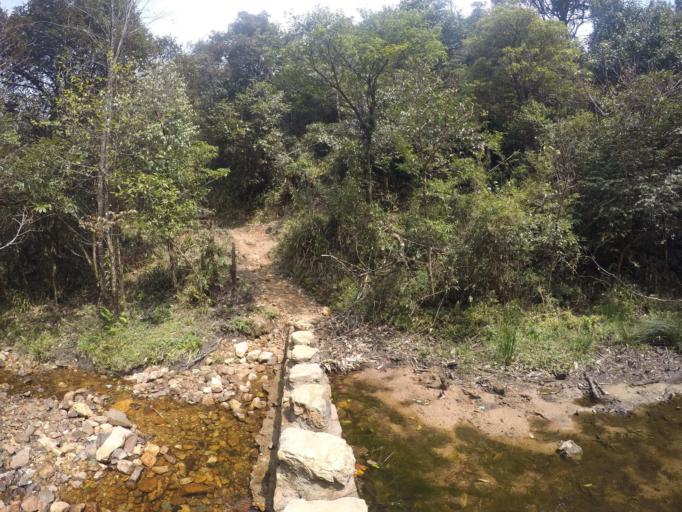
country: VN
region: Lao Cai
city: Sa Pa
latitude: 22.3502
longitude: 103.7744
